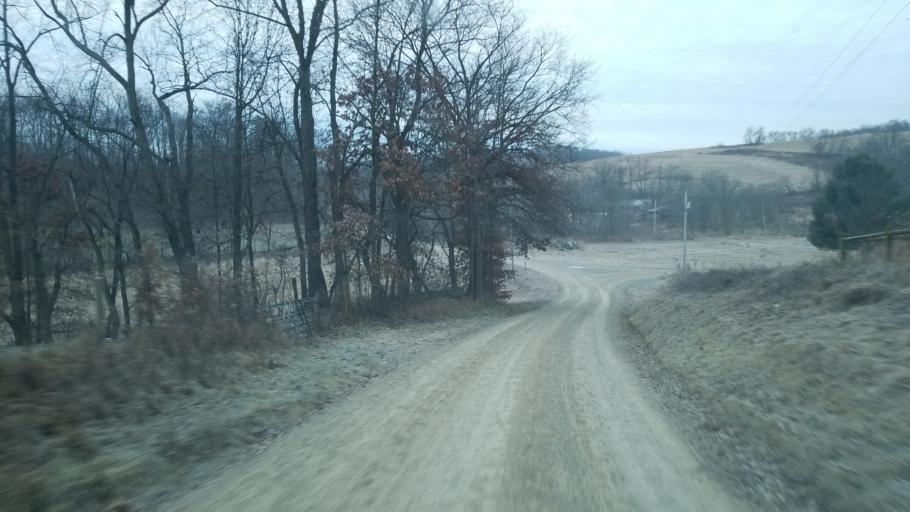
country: US
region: Ohio
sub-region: Holmes County
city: Millersburg
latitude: 40.4551
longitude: -81.8472
